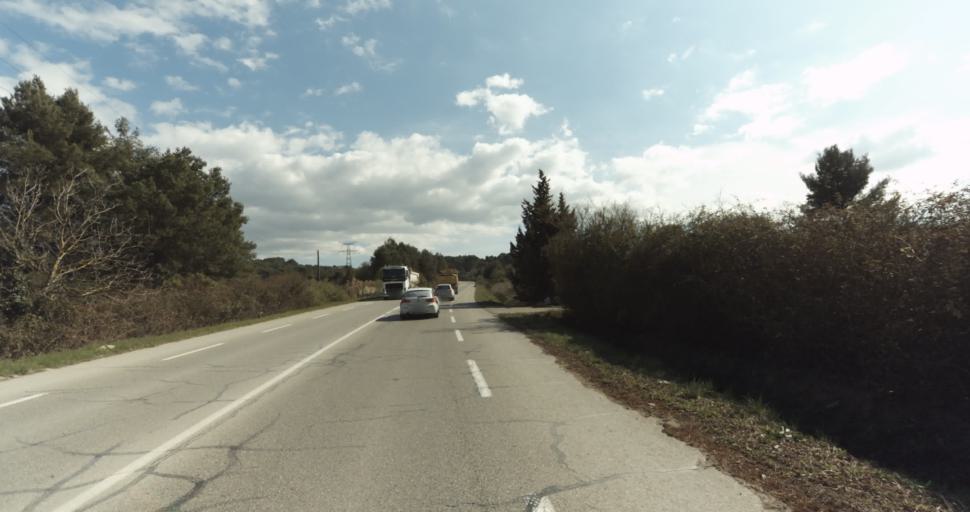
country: FR
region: Provence-Alpes-Cote d'Azur
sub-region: Departement des Bouches-du-Rhone
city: Gardanne
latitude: 43.4619
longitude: 5.4881
